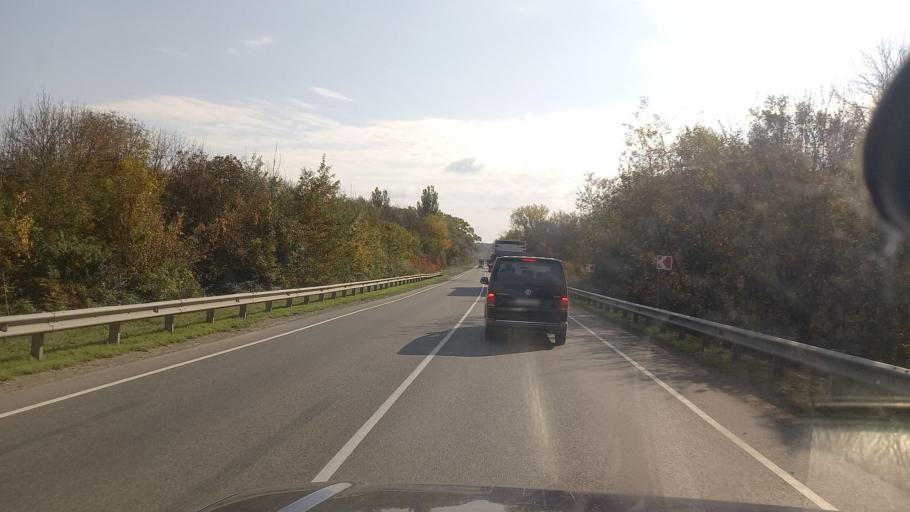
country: RU
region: Krasnodarskiy
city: Abinsk
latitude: 44.8442
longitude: 38.1531
